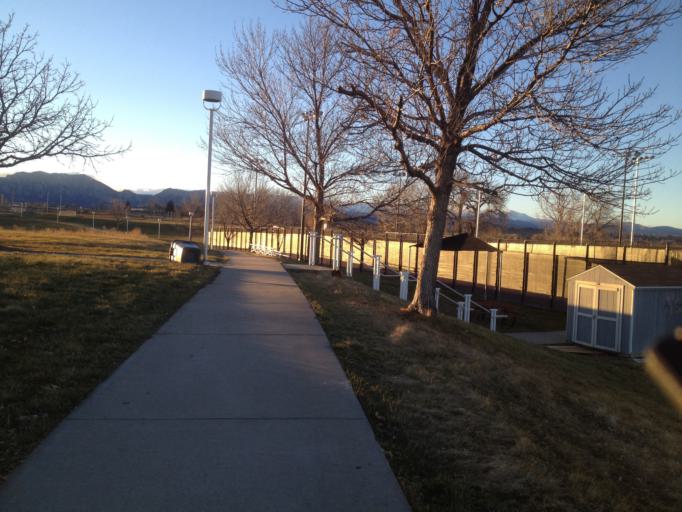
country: US
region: Colorado
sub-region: Boulder County
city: Louisville
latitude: 39.9534
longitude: -105.1413
